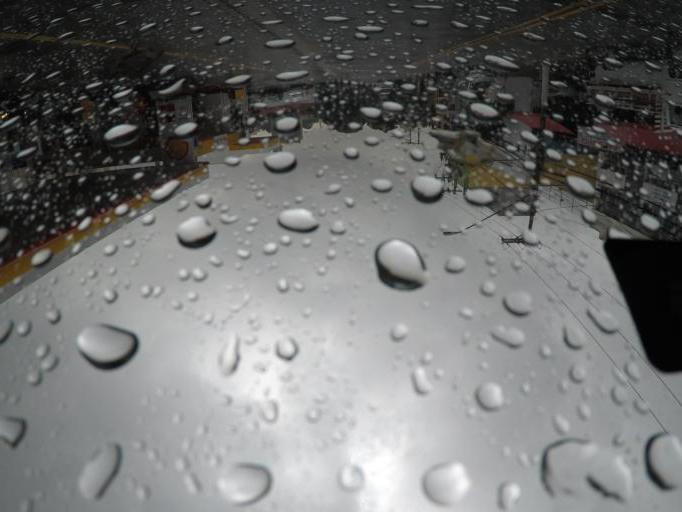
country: BR
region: Sao Paulo
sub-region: Diadema
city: Diadema
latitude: -23.6393
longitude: -46.6430
